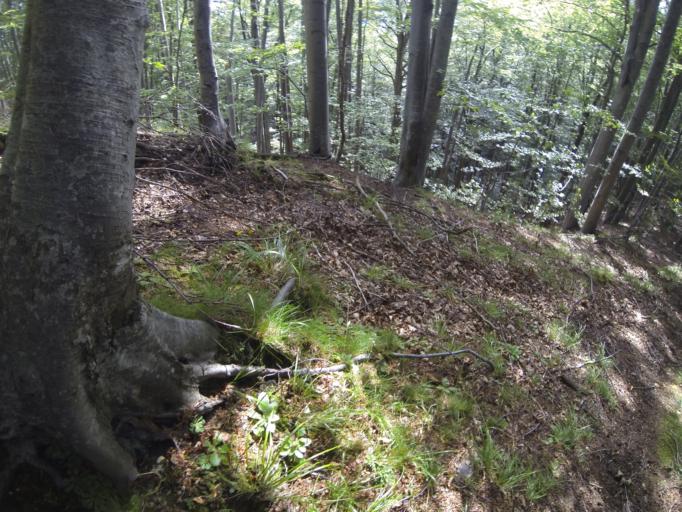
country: RO
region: Valcea
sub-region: Comuna Barbatesti
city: Barbatesti
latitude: 45.2591
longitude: 24.1528
